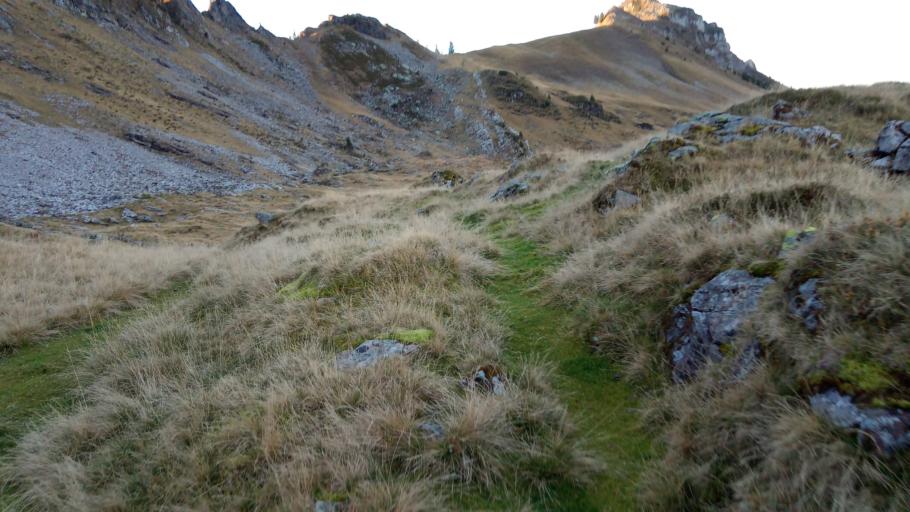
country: CH
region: Bern
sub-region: Interlaken-Oberhasli District
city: Beatenberg
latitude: 46.7478
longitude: 7.7915
